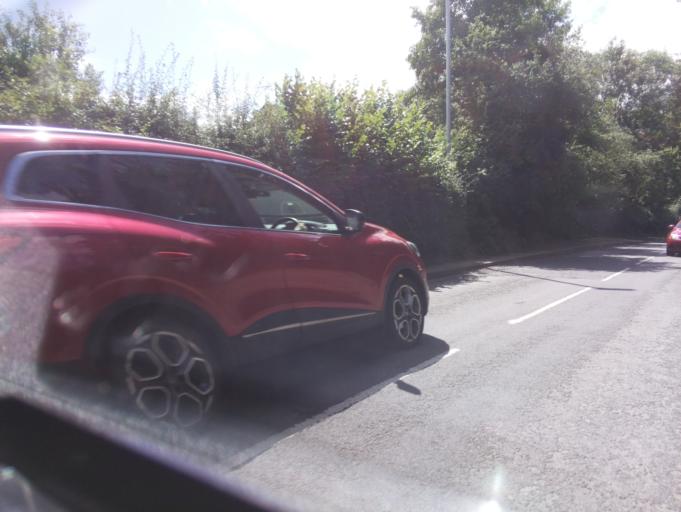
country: GB
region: England
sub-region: Nottinghamshire
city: Lowdham
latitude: 53.0126
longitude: -1.0145
